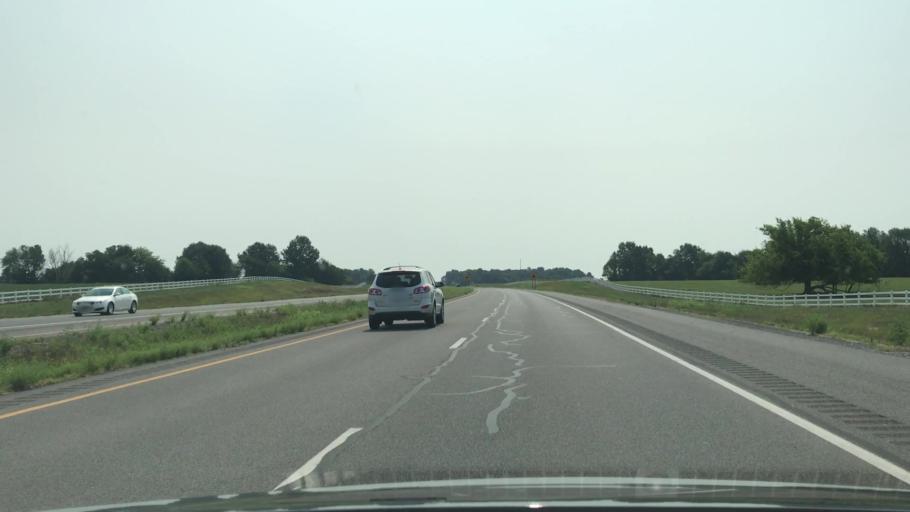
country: US
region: Kentucky
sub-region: Graves County
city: Mayfield
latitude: 36.6798
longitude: -88.5295
